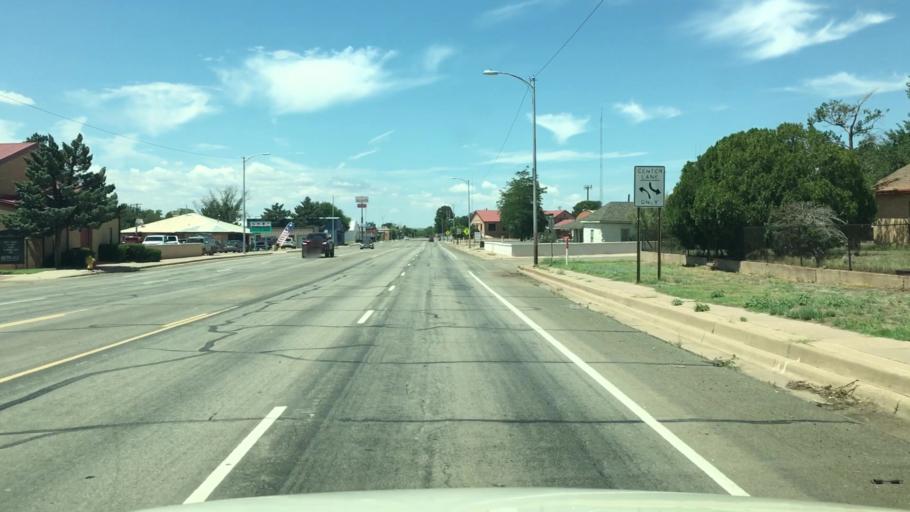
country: US
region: New Mexico
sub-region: De Baca County
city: Fort Sumner
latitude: 34.4700
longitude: -104.2399
